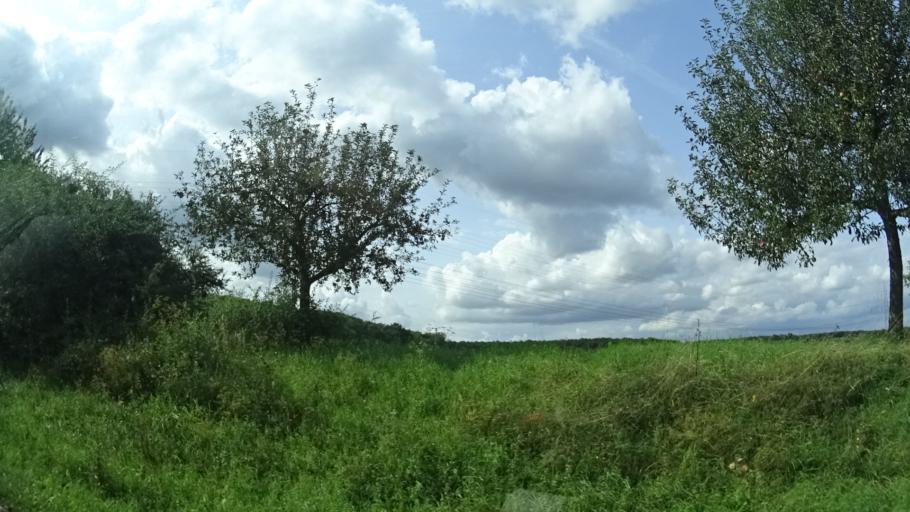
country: DE
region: Bavaria
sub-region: Regierungsbezirk Unterfranken
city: Bergrheinfeld
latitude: 49.9984
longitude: 10.1644
